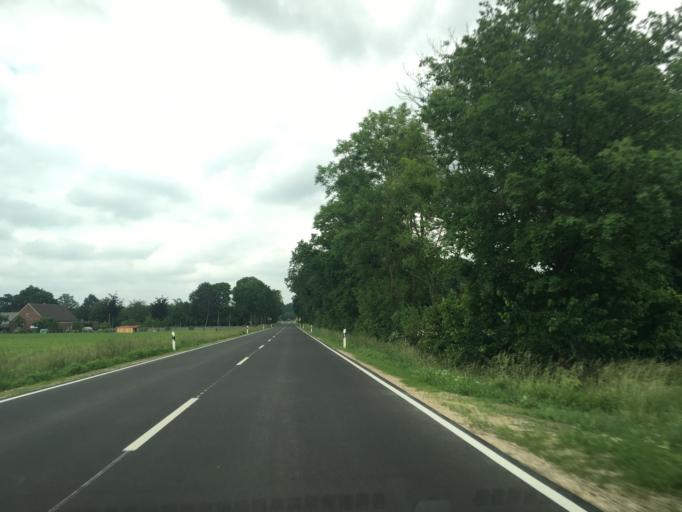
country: DE
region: North Rhine-Westphalia
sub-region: Regierungsbezirk Munster
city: Horstmar
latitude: 52.1093
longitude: 7.3321
